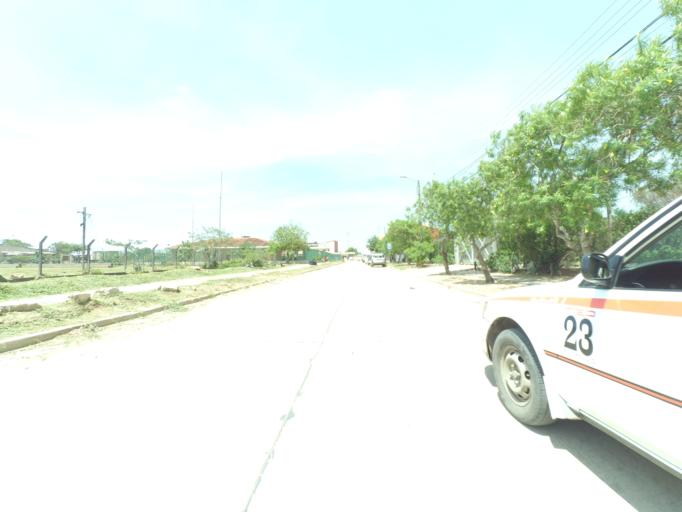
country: BO
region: Santa Cruz
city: Santa Cruz de la Sierra
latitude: -17.8117
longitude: -63.2145
